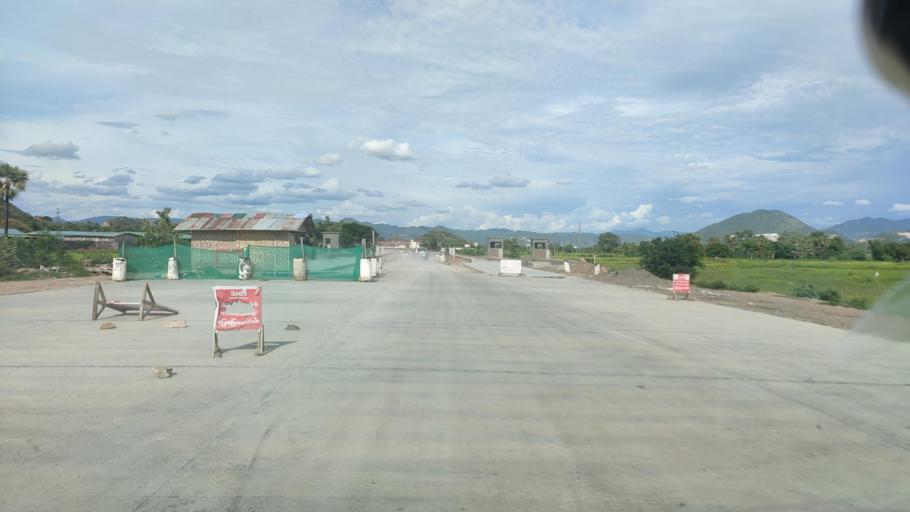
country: MM
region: Mandalay
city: Kyaukse
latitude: 21.5993
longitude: 96.1776
